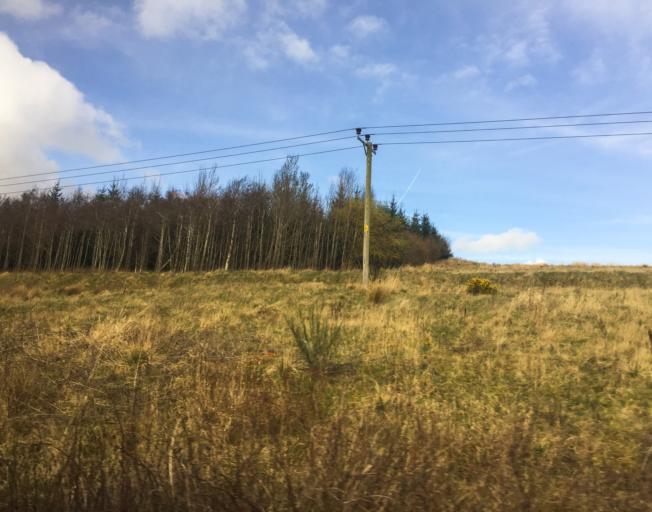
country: GB
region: Scotland
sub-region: North Lanarkshire
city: Glenboig
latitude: 55.8806
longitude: -4.0529
